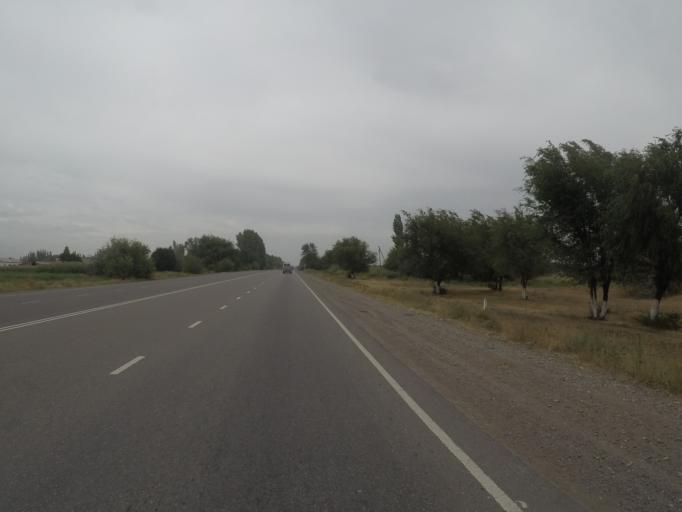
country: KG
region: Chuy
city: Bystrovka
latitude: 42.8193
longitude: 75.5744
